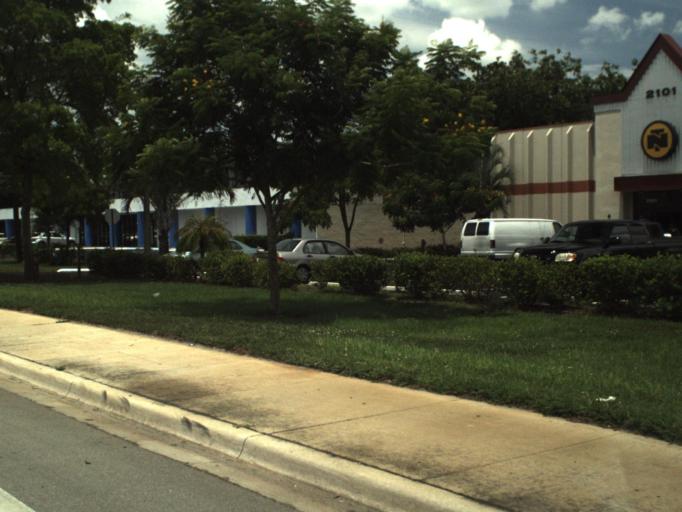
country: US
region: Florida
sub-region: Broward County
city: Pompano Beach
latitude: 26.2315
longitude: -80.1518
